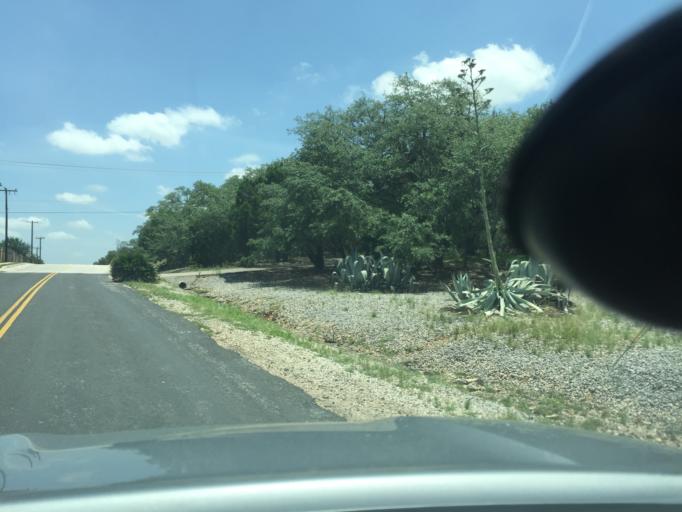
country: US
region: Texas
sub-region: Bexar County
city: Timberwood Park
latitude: 29.6863
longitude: -98.4797
